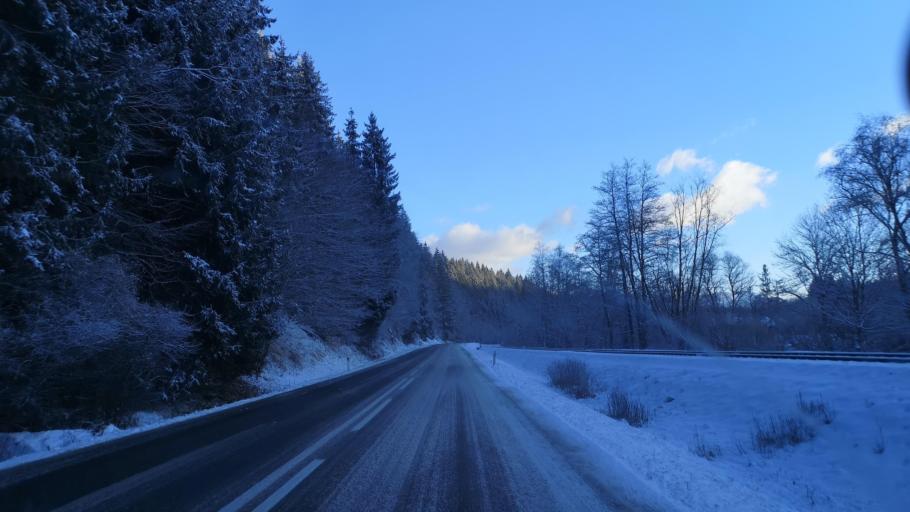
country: SK
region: Banskobystricky
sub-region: Okres Banska Bystrica
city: Brezno
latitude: 48.8324
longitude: 19.7786
